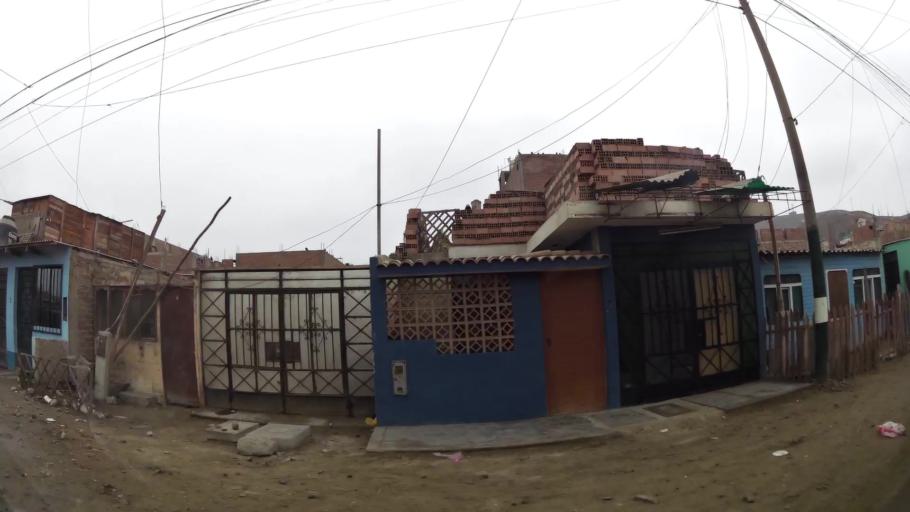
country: PE
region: Lima
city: Ventanilla
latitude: -11.8799
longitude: -77.1327
